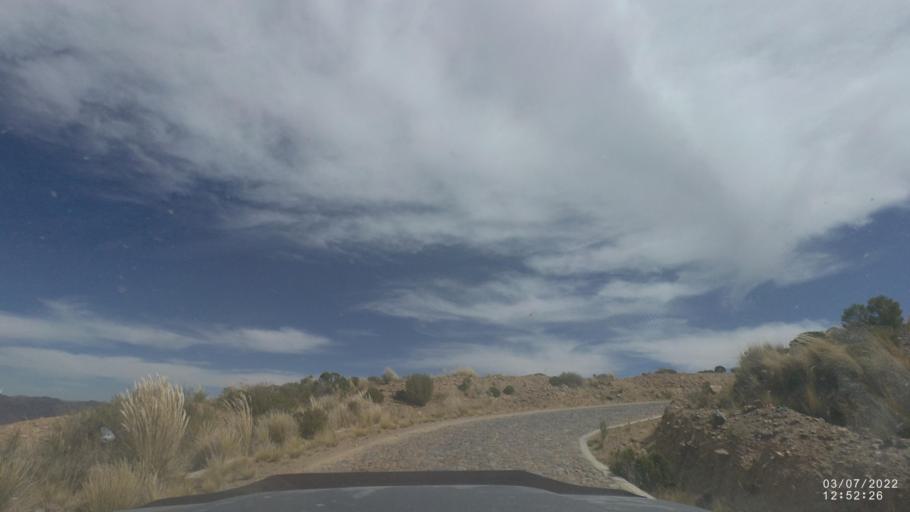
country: BO
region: Cochabamba
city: Irpa Irpa
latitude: -17.7497
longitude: -66.6612
